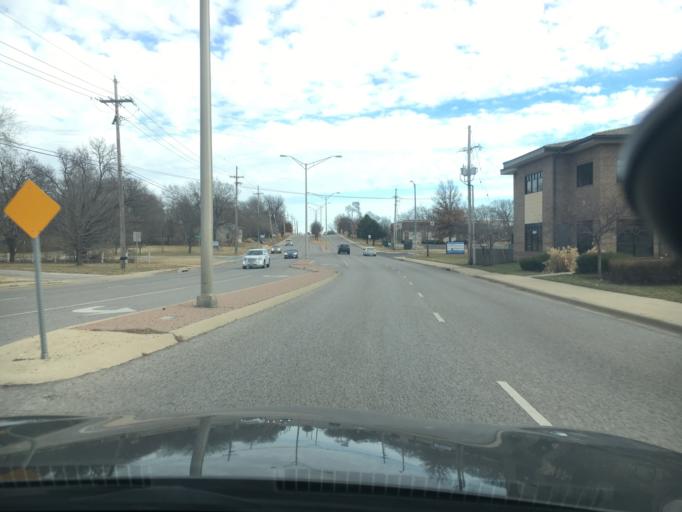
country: US
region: Kansas
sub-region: Johnson County
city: Lenexa
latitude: 38.8546
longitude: -94.6651
